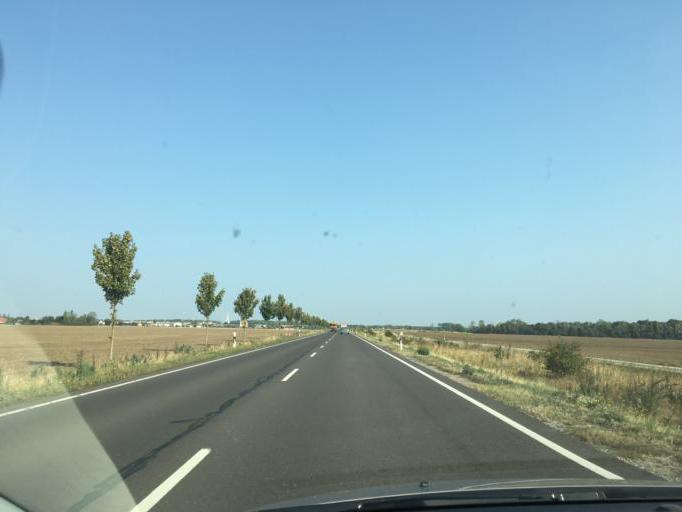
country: DE
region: Saxony-Anhalt
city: Schonebeck
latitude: 51.9989
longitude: 11.7741
